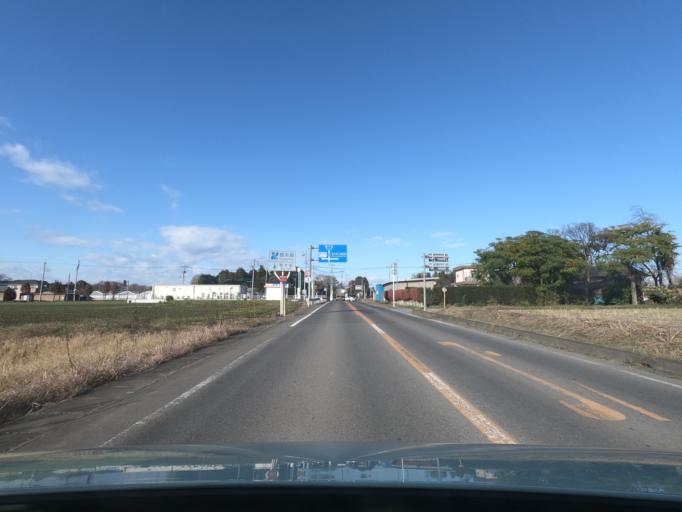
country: JP
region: Ibaraki
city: Koga
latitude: 36.2222
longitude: 139.7700
